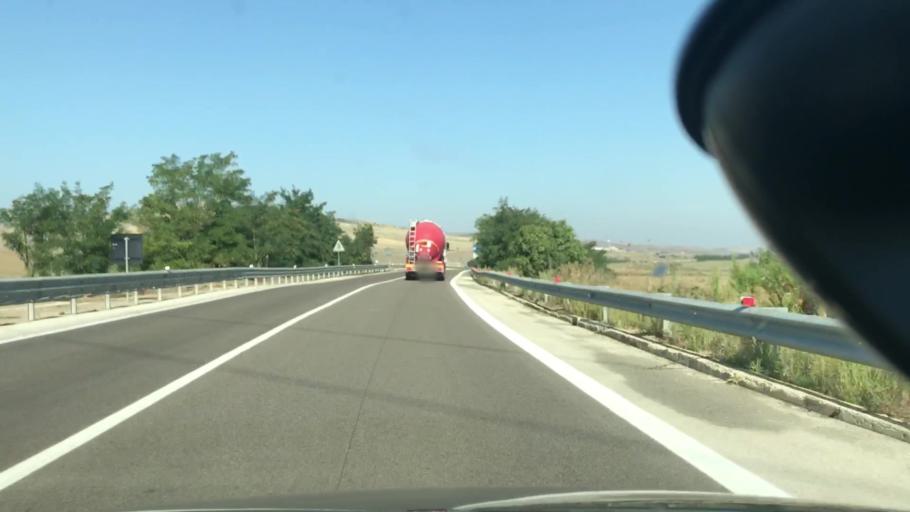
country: IT
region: Basilicate
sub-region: Provincia di Matera
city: Irsina
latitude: 40.7889
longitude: 16.2874
